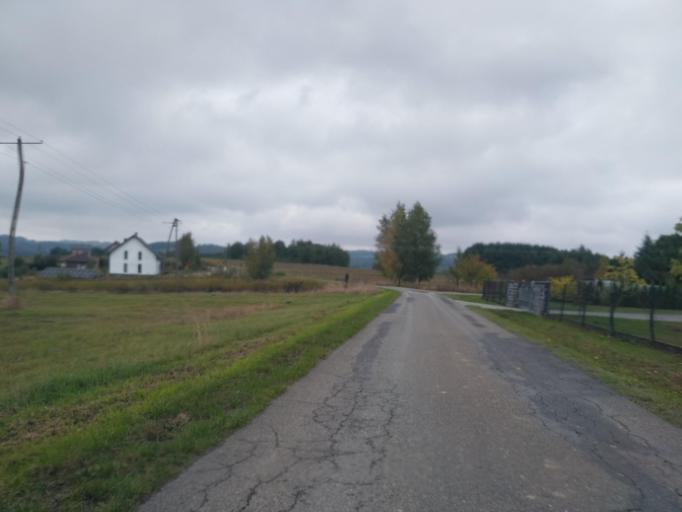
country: PL
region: Subcarpathian Voivodeship
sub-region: Powiat debicki
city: Brzostek
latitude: 49.9292
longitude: 21.4490
